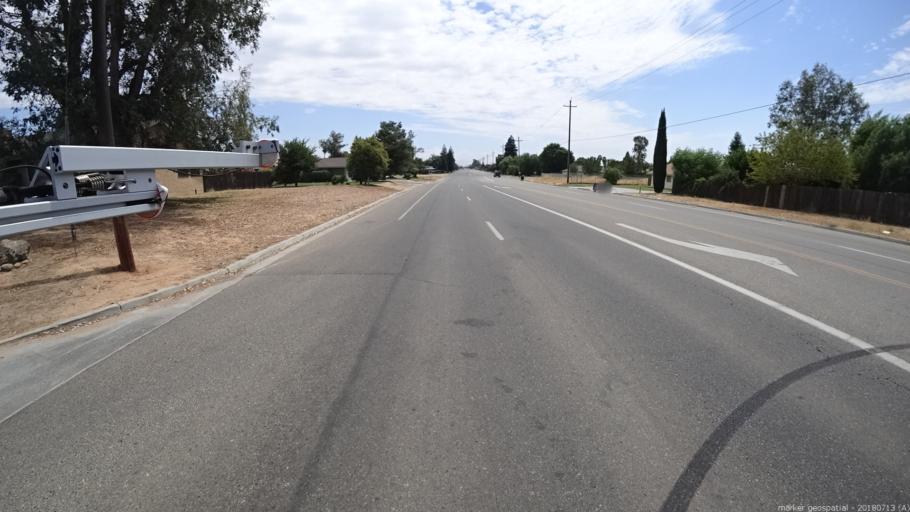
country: US
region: California
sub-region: Madera County
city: Madera Acres
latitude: 36.9964
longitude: -120.0821
